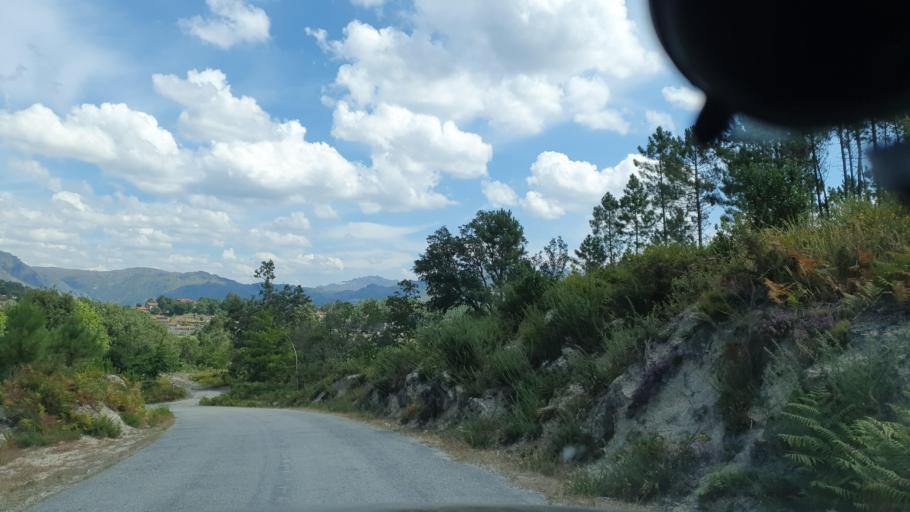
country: PT
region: Braga
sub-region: Vieira do Minho
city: Vieira do Minho
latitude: 41.7023
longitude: -8.0573
